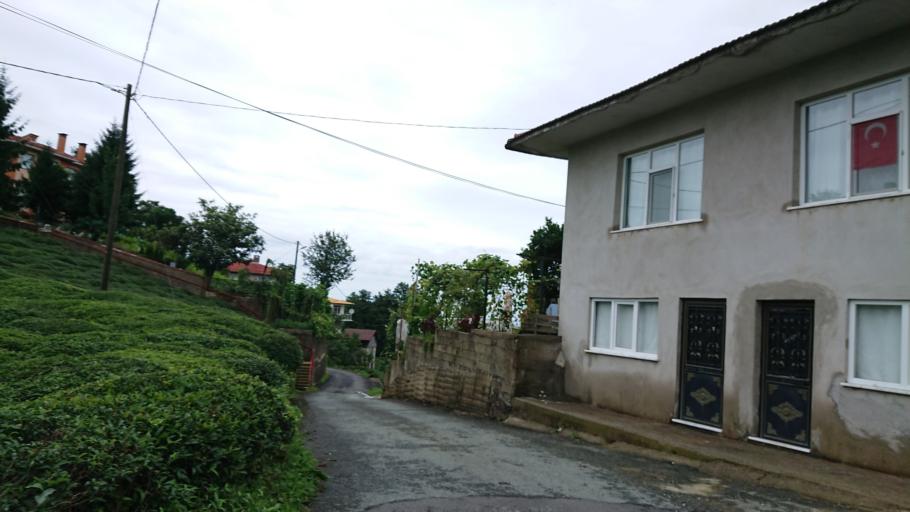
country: TR
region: Rize
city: Rize
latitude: 40.9840
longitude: 40.4852
